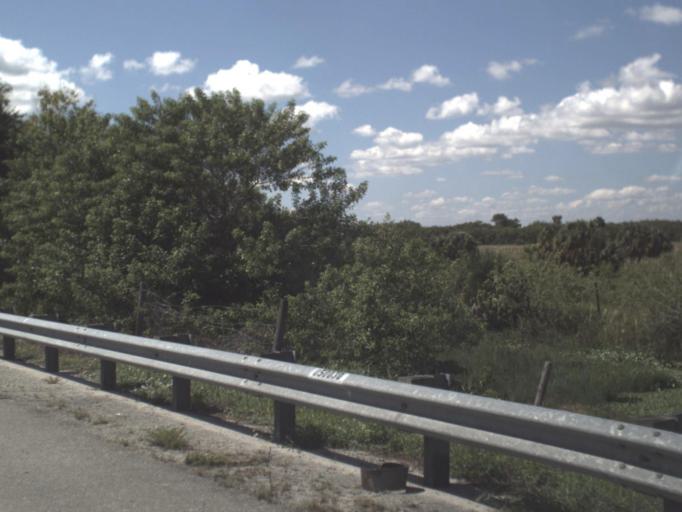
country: US
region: Florida
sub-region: Glades County
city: Buckhead Ridge
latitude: 27.1307
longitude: -80.9026
